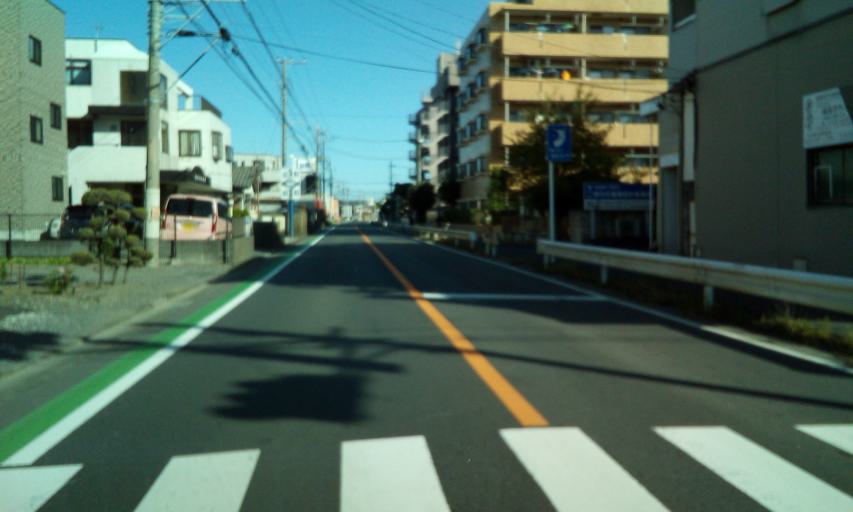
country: JP
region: Chiba
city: Nagareyama
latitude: 35.8532
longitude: 139.8828
